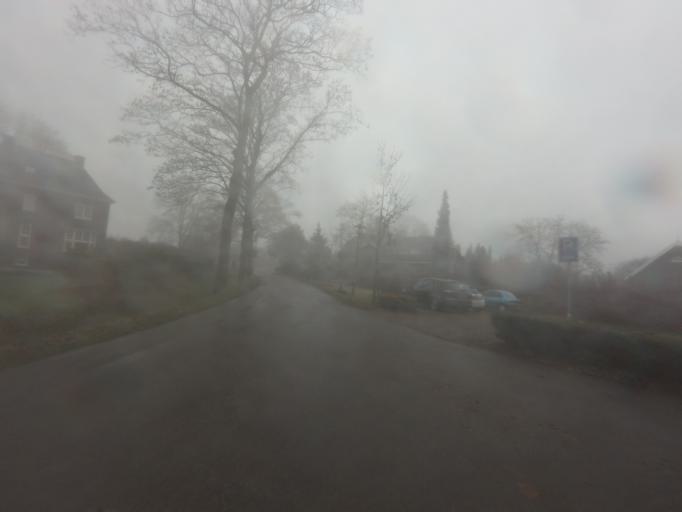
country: NL
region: Gelderland
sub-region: Gemeente Zaltbommel
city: Zaltbommel
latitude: 51.8022
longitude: 5.2060
